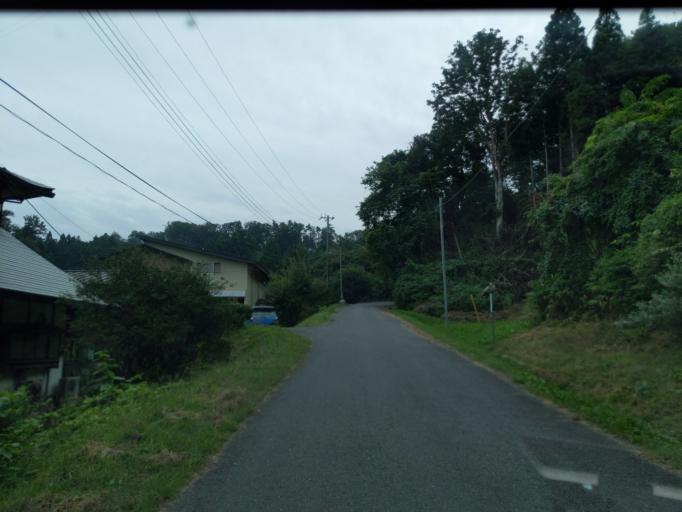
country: JP
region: Iwate
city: Ichinoseki
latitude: 38.9543
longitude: 141.1181
